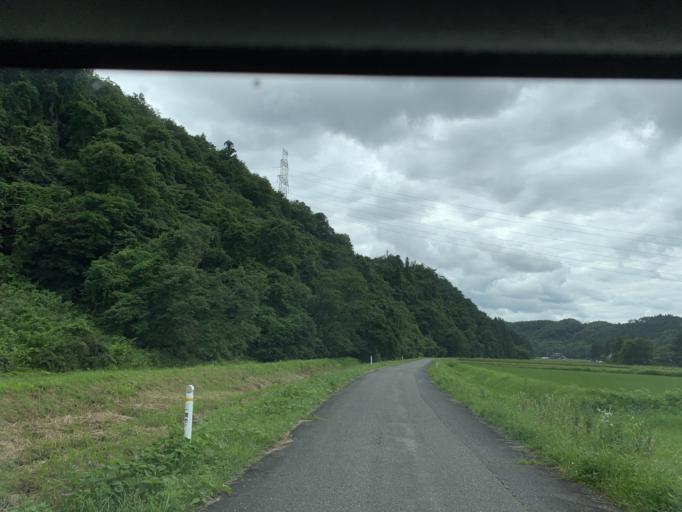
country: JP
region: Iwate
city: Ichinoseki
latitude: 38.9459
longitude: 141.0203
